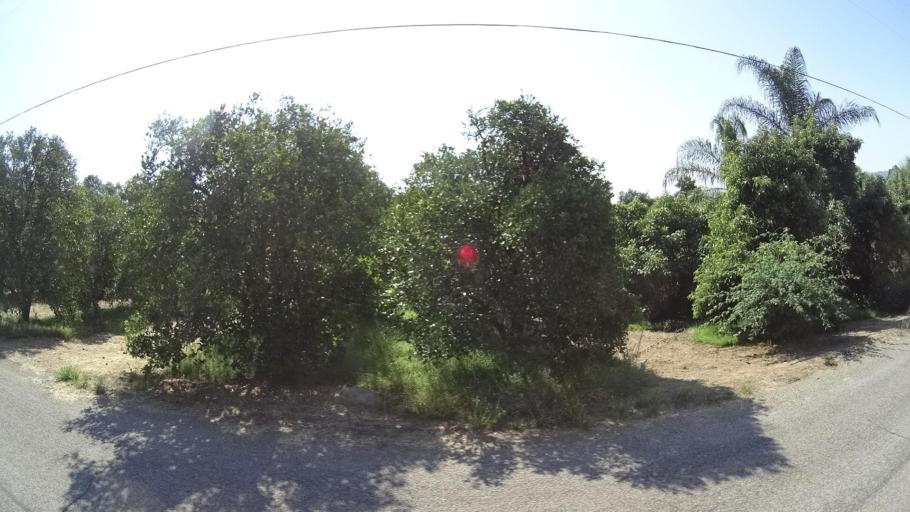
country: US
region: California
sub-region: San Diego County
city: Valley Center
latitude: 33.3445
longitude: -117.0076
